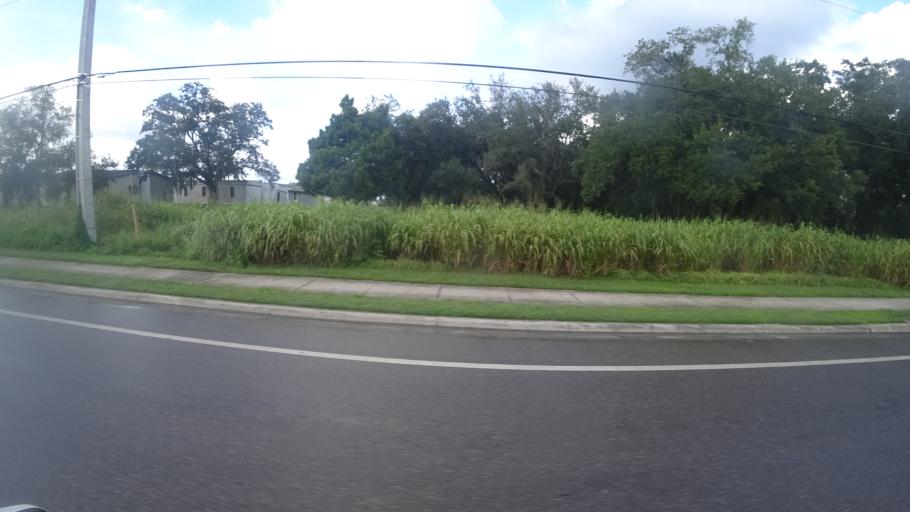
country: US
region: Florida
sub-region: Manatee County
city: Memphis
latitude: 27.5284
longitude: -82.5491
